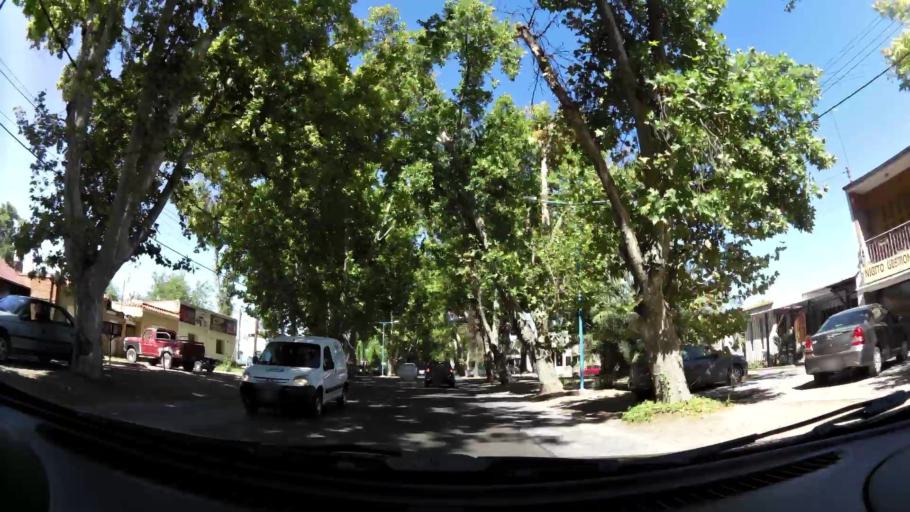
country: AR
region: Mendoza
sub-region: Departamento de Godoy Cruz
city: Godoy Cruz
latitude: -32.9484
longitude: -68.8437
